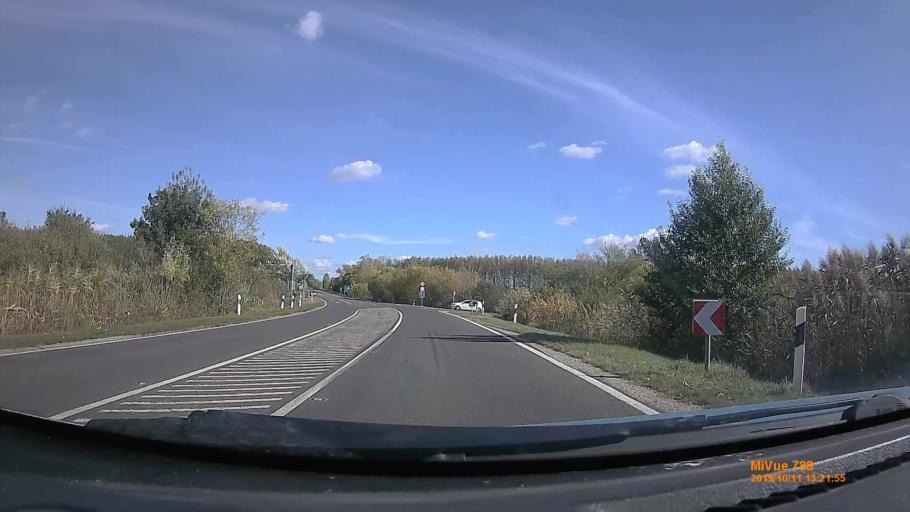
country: HU
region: Hajdu-Bihar
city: Balmazujvaros
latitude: 47.5520
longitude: 21.3261
